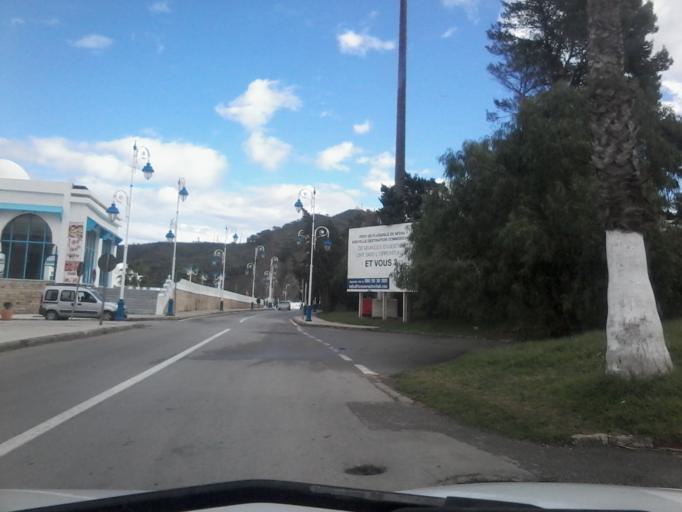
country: MA
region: Tanger-Tetouan
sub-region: Tetouan
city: Martil
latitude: 35.6823
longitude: -5.3169
